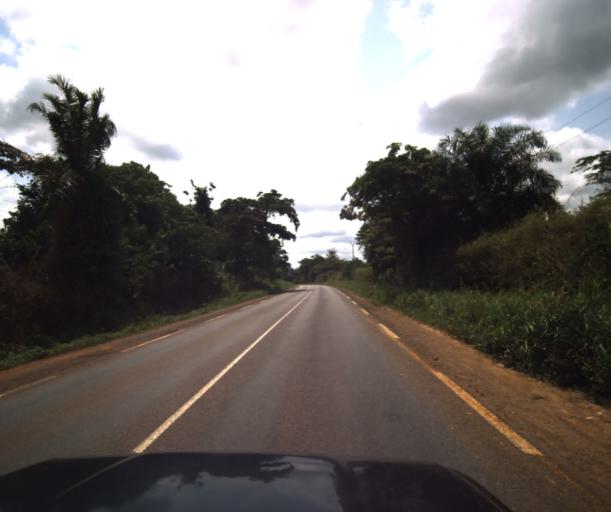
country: CM
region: Centre
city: Eseka
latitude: 3.8862
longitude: 10.8008
